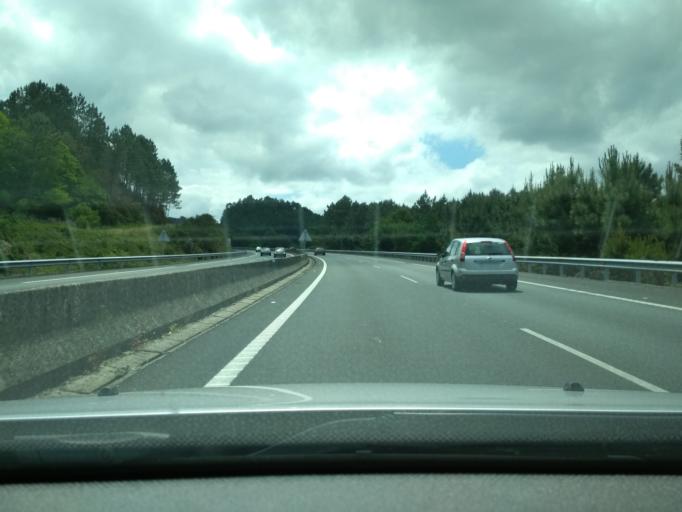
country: ES
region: Galicia
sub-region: Provincia de Pontevedra
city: Portas
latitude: 42.5838
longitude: -8.6757
